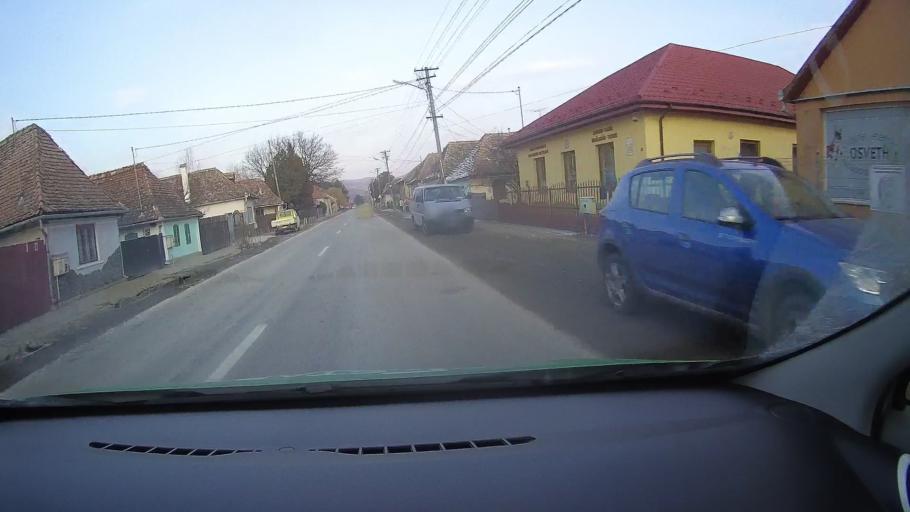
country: RO
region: Harghita
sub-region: Oras Cristuru Secuiesc
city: Cristuru Secuiesc
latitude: 46.2917
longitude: 25.0403
